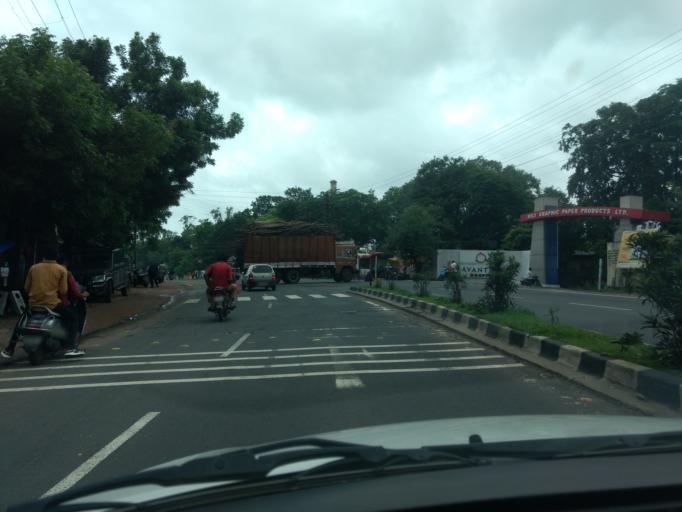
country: IN
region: Maharashtra
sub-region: Chandrapur
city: Ballalpur
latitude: 19.8695
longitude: 79.3404
